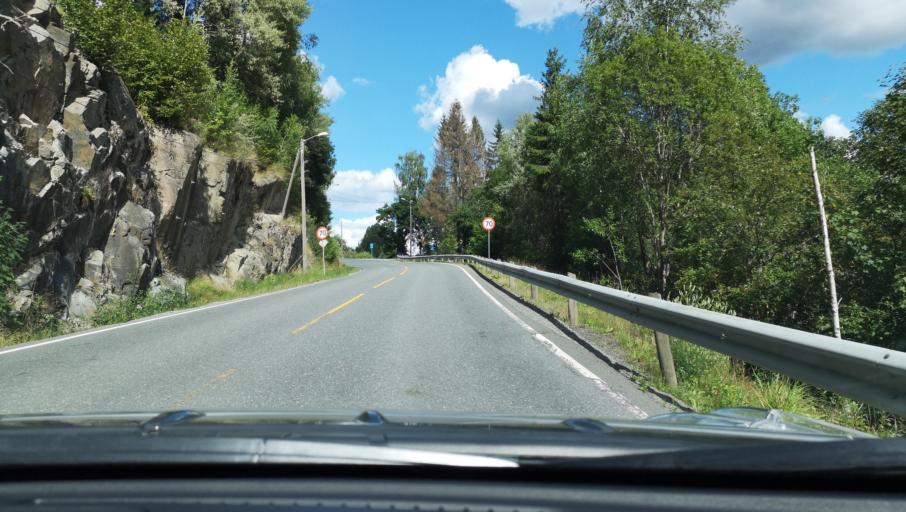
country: NO
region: Ostfold
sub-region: Hobol
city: Tomter
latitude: 59.6547
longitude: 11.0005
